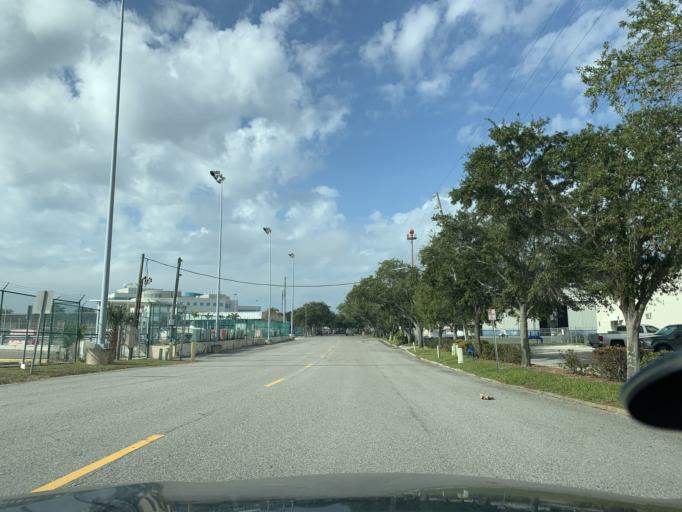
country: US
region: Florida
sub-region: Pinellas County
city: Saint Petersburg
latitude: 27.7625
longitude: -82.6303
